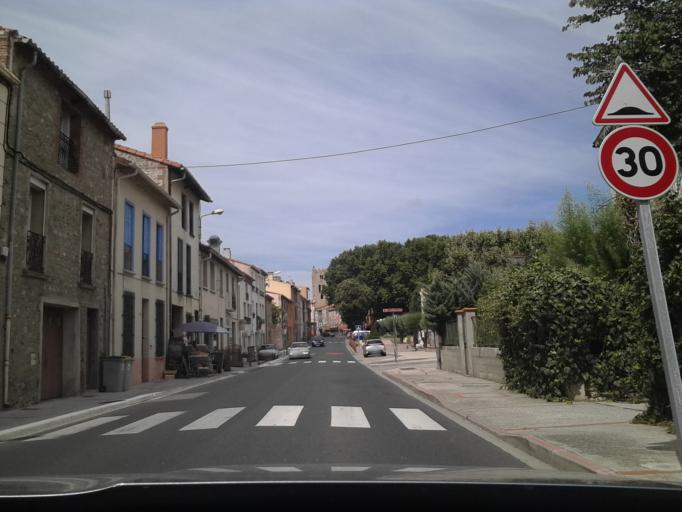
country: FR
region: Languedoc-Roussillon
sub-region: Departement des Pyrenees-Orientales
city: Millas
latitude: 42.6913
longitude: 2.6999
